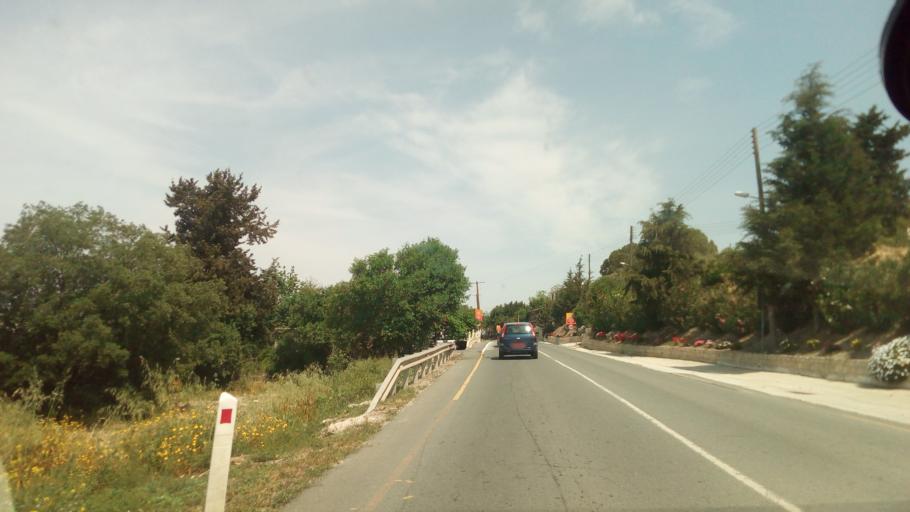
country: CY
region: Pafos
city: Tala
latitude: 34.8876
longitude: 32.4813
